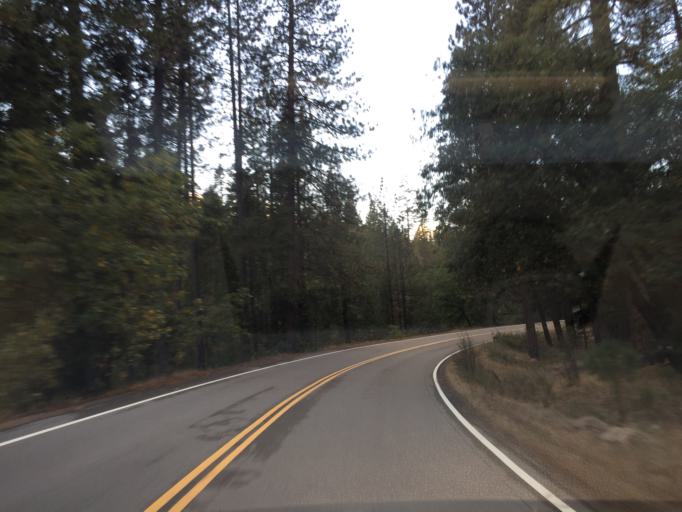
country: US
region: California
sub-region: Madera County
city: Ahwahnee
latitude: 37.5430
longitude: -119.6708
